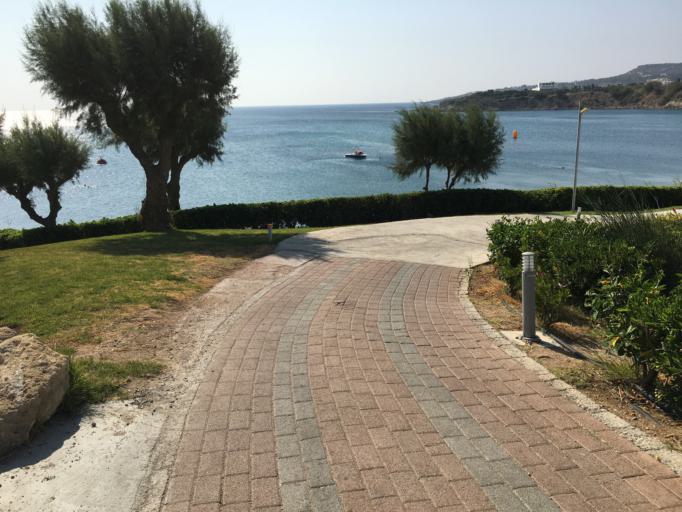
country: GR
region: South Aegean
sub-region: Nomos Dodekanisou
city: Rodos
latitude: 36.4057
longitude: 28.2281
